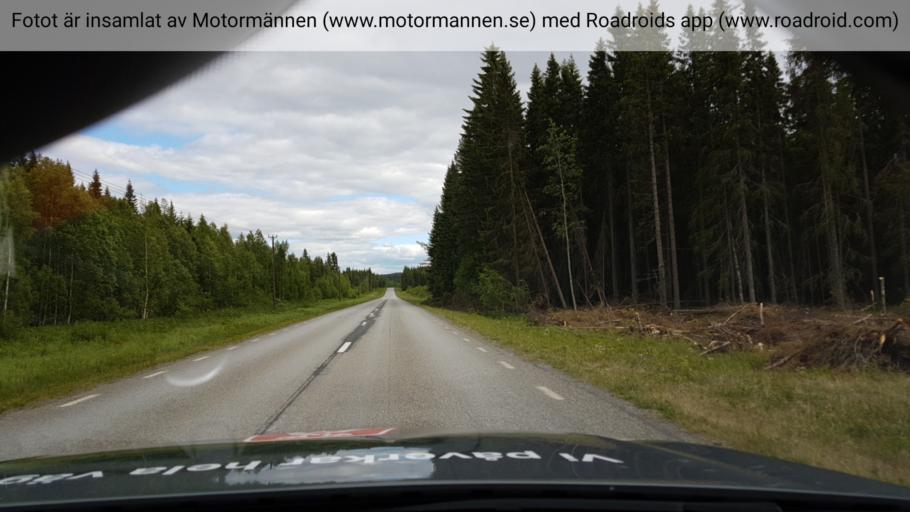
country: SE
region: Jaemtland
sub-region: Stroemsunds Kommun
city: Stroemsund
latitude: 63.9301
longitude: 15.5021
